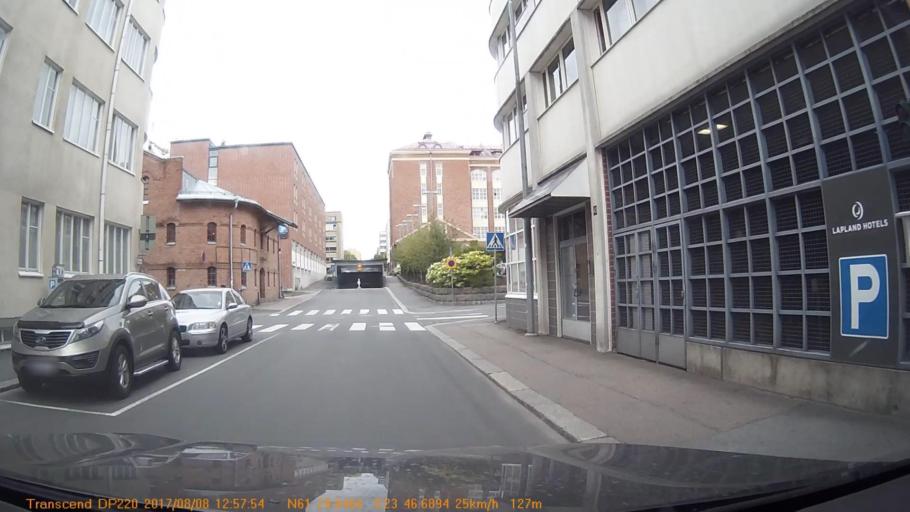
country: FI
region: Pirkanmaa
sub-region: Tampere
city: Tampere
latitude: 61.4976
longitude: 23.7782
